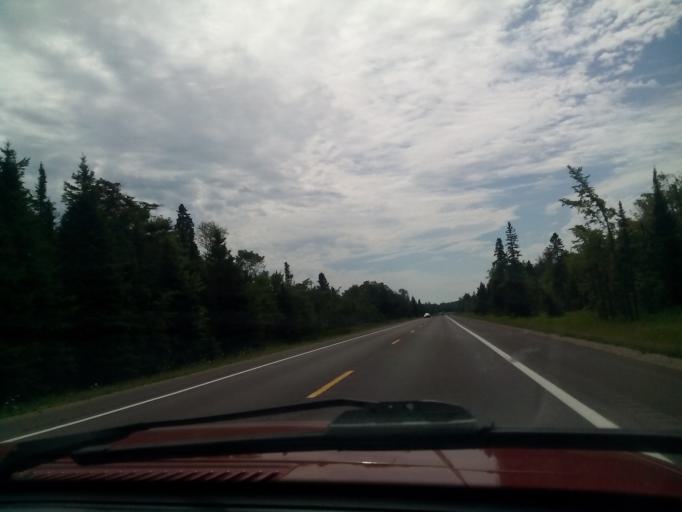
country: US
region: Michigan
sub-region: Schoolcraft County
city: Manistique
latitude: 46.0706
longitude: -85.9584
